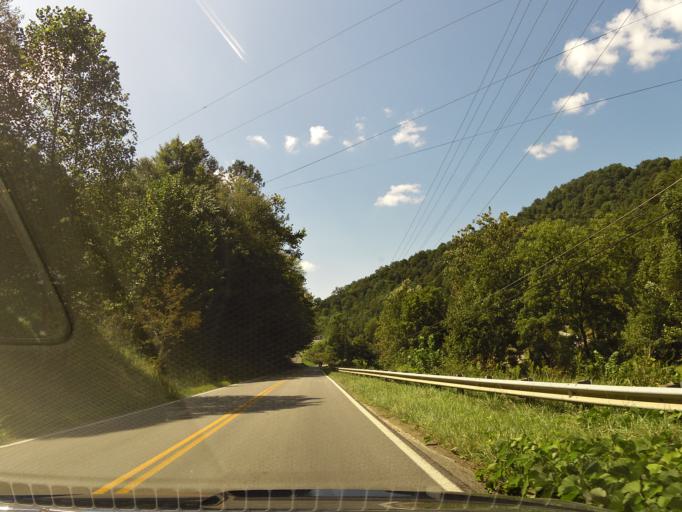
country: US
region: Kentucky
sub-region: Harlan County
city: Loyall
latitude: 36.9862
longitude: -83.3958
